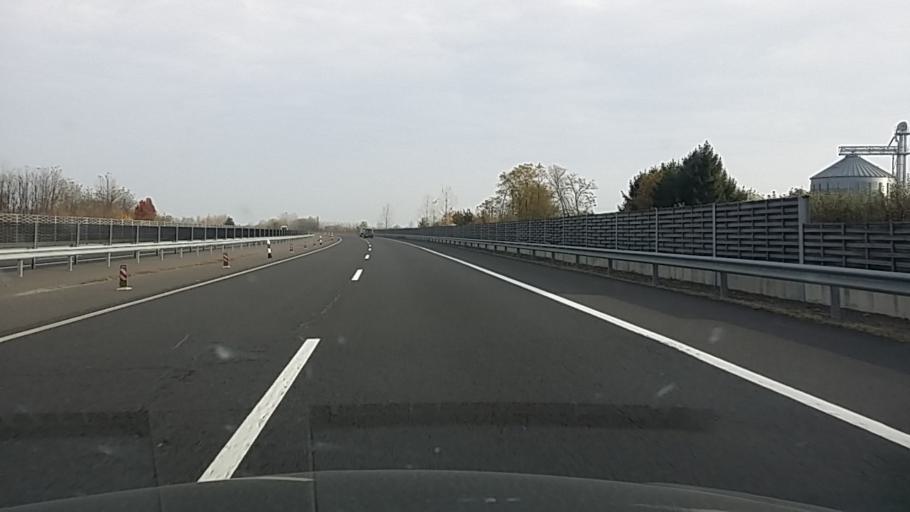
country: HU
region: Szabolcs-Szatmar-Bereg
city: Kalmanhaza
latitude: 47.8969
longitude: 21.6070
